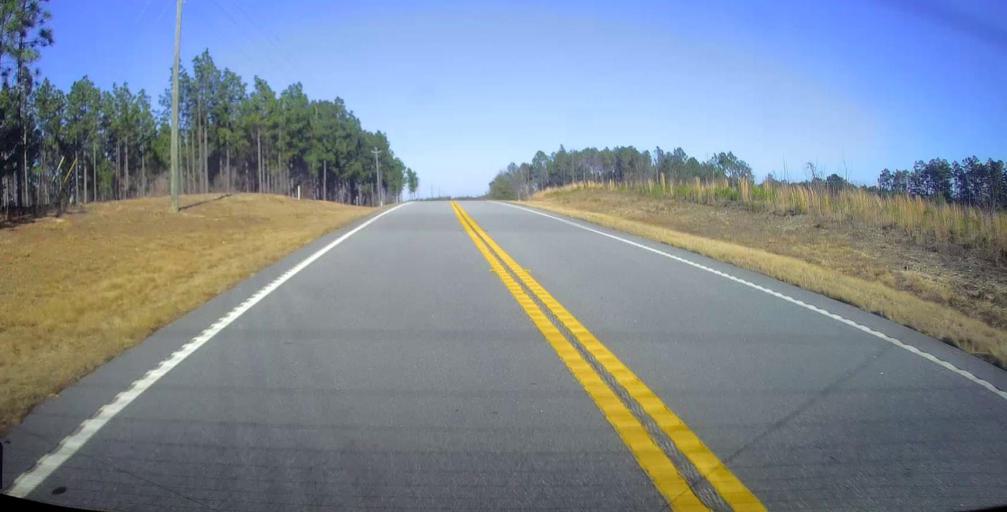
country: US
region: Georgia
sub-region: Taylor County
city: Butler
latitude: 32.5783
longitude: -84.2103
